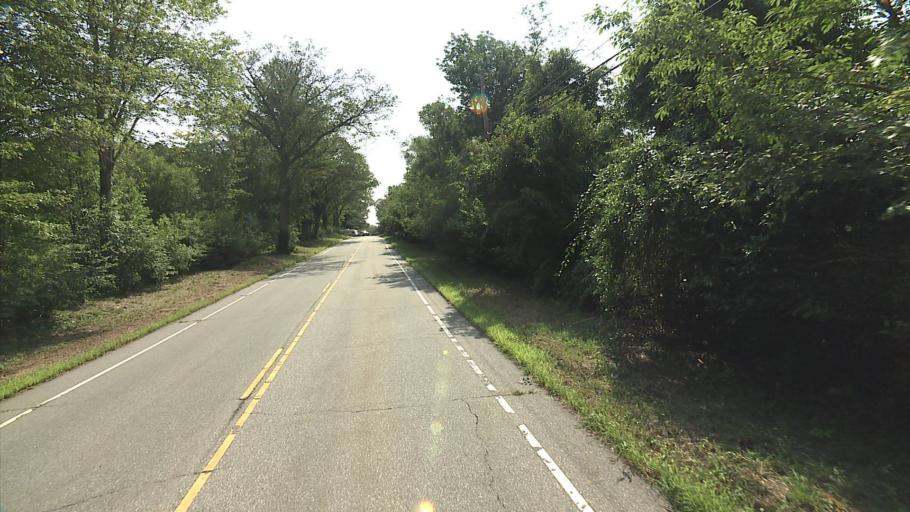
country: US
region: Connecticut
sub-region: New London County
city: Colchester
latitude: 41.5719
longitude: -72.2366
